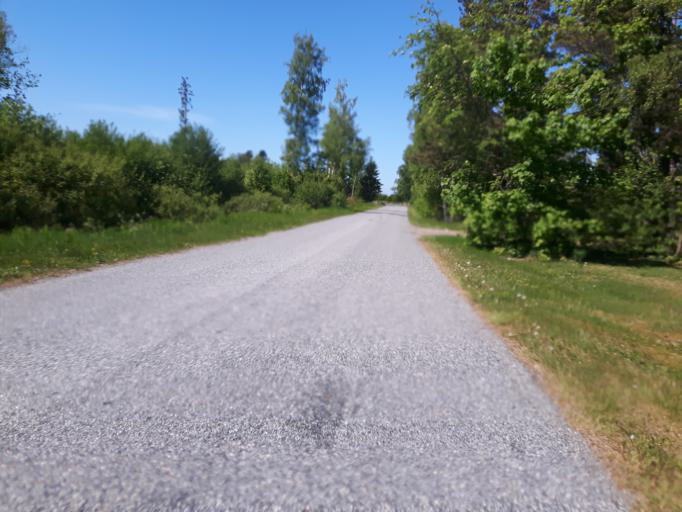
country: EE
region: Laeaene-Virumaa
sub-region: Haljala vald
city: Haljala
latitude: 59.5638
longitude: 26.3097
